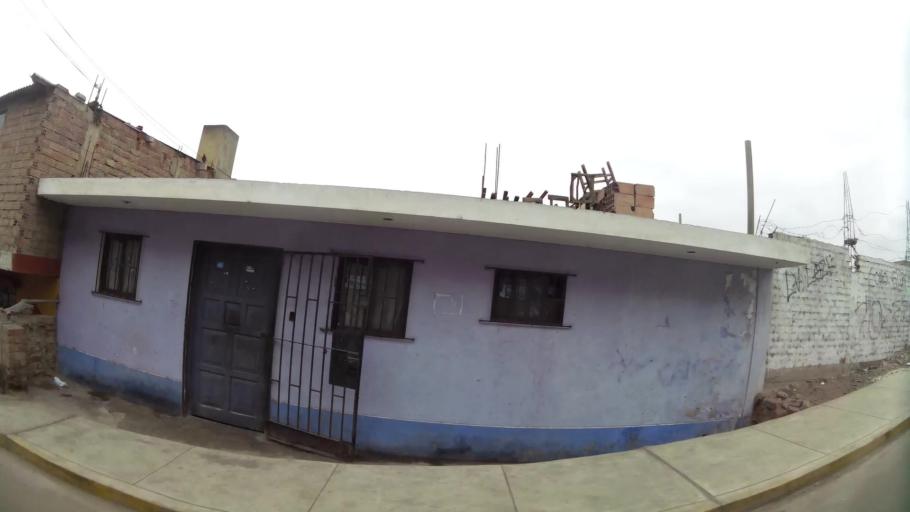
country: PE
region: Lima
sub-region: Lima
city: Surco
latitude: -12.1842
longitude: -77.0141
